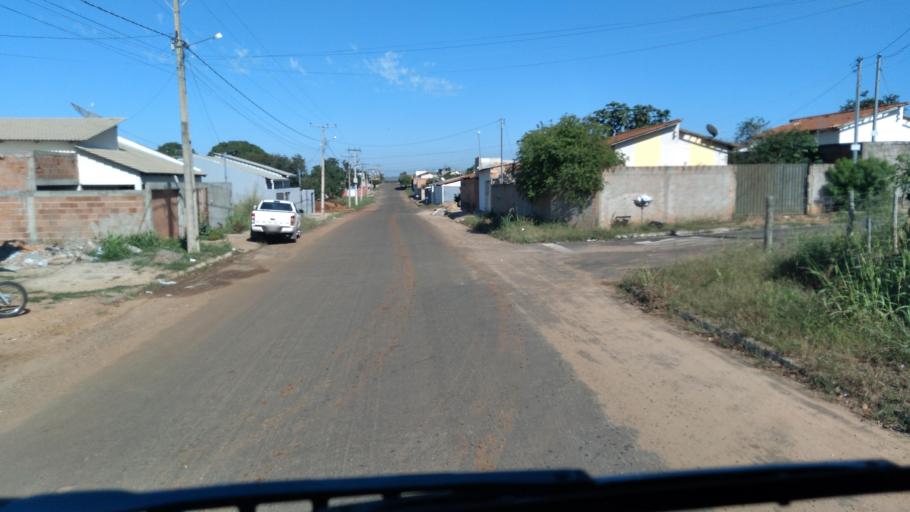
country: BR
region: Goias
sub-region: Mineiros
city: Mineiros
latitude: -17.5763
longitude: -52.5726
